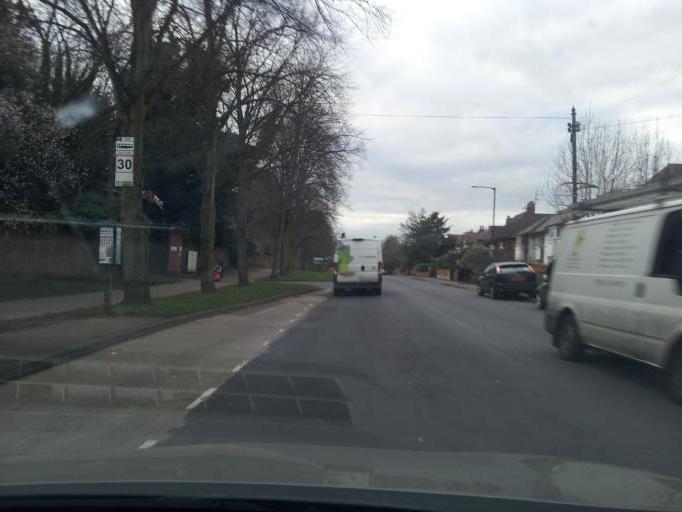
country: GB
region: England
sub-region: Nottingham
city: Nottingham
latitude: 52.9542
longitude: -1.2119
